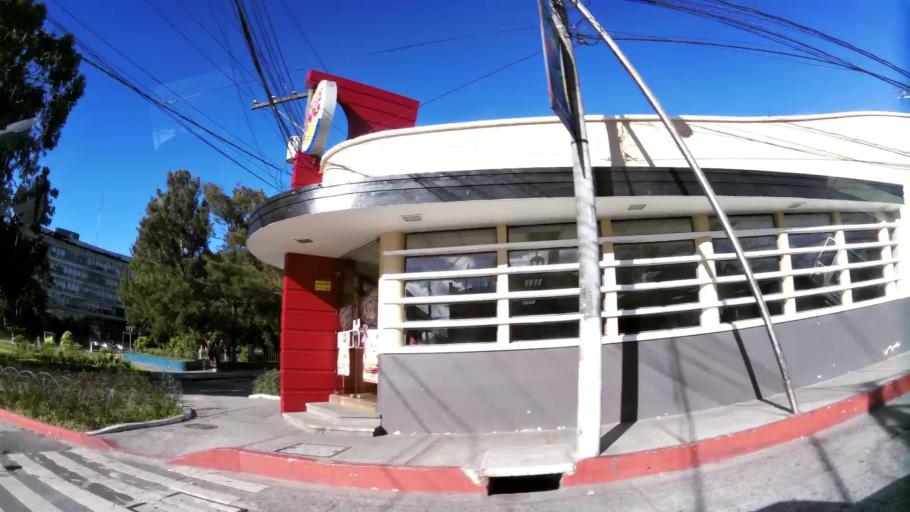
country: GT
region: Guatemala
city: Guatemala City
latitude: 14.6279
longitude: -90.5145
